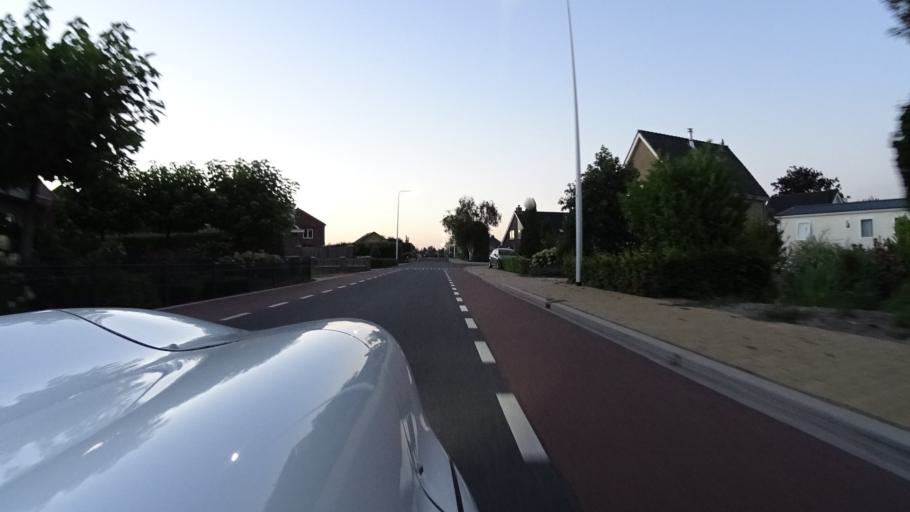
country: NL
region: South Holland
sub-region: Gemeente Kaag en Braassem
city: Oude Wetering
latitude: 52.1942
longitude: 4.6201
